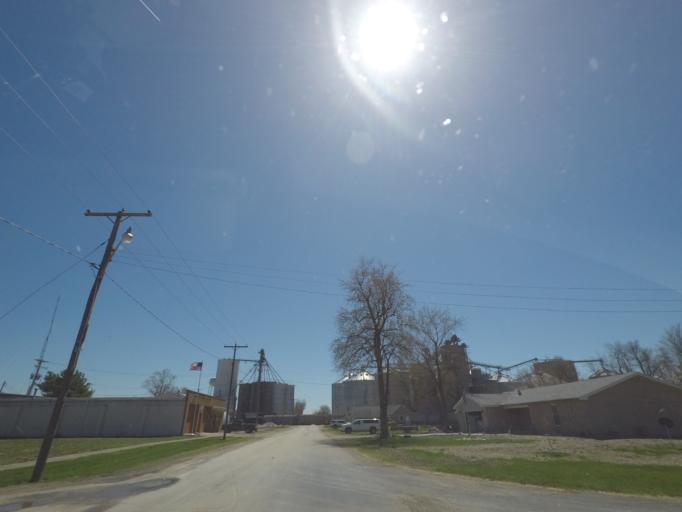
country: US
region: Illinois
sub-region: Macon County
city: Warrensburg
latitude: 39.9675
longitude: -89.1627
